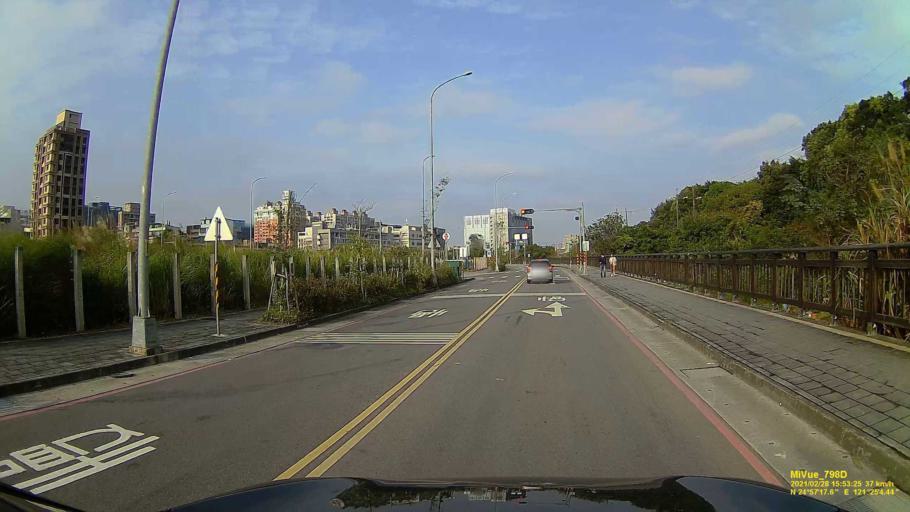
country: TW
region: Taipei
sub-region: Taipei
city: Banqiao
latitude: 24.9551
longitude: 121.4181
